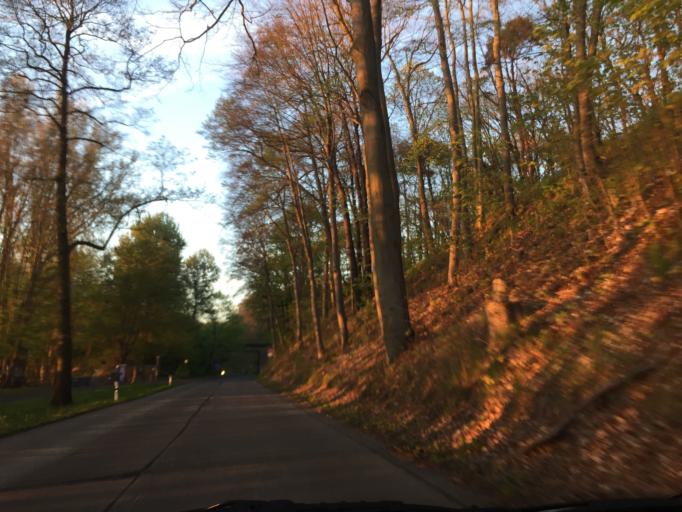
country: DE
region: Brandenburg
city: Michendorf
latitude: 52.3625
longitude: 13.0271
